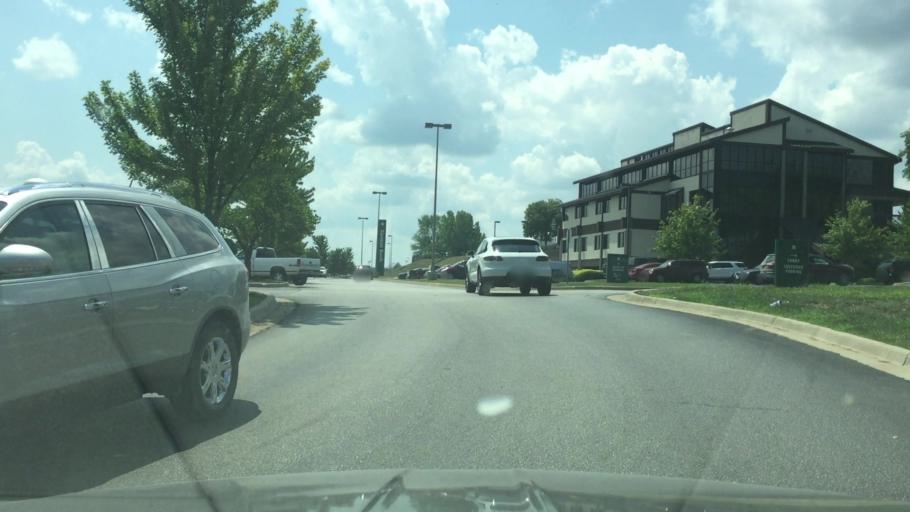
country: US
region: Missouri
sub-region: Miller County
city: Lake Ozark
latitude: 38.1619
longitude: -92.6059
